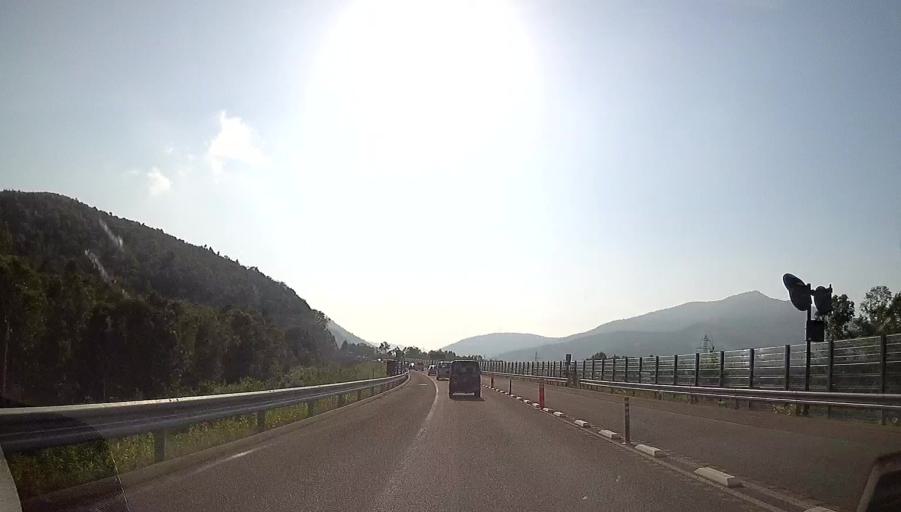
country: JP
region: Hokkaido
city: Shimo-furano
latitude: 43.0530
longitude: 142.6421
